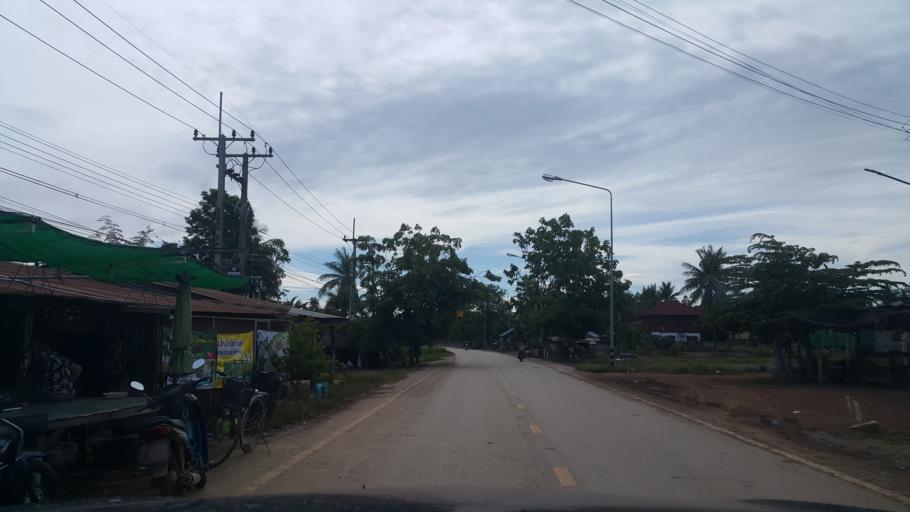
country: TH
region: Sukhothai
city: Si Nakhon
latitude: 17.2745
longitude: 99.9880
